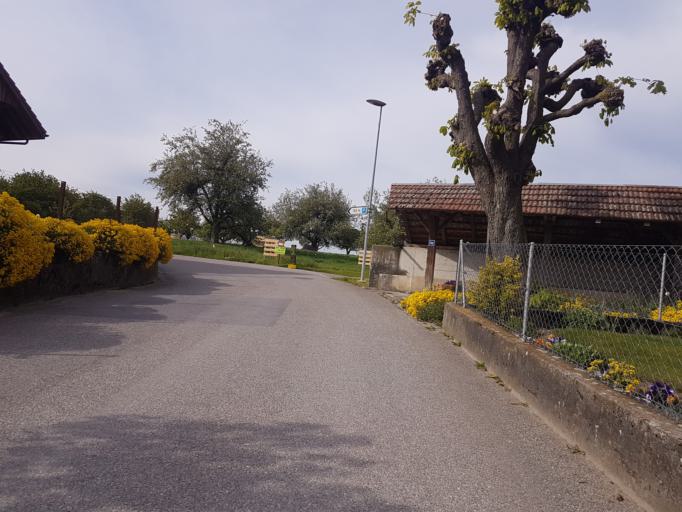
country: CH
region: Bern
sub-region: Seeland District
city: Tauffelen
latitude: 47.0954
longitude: 7.2086
